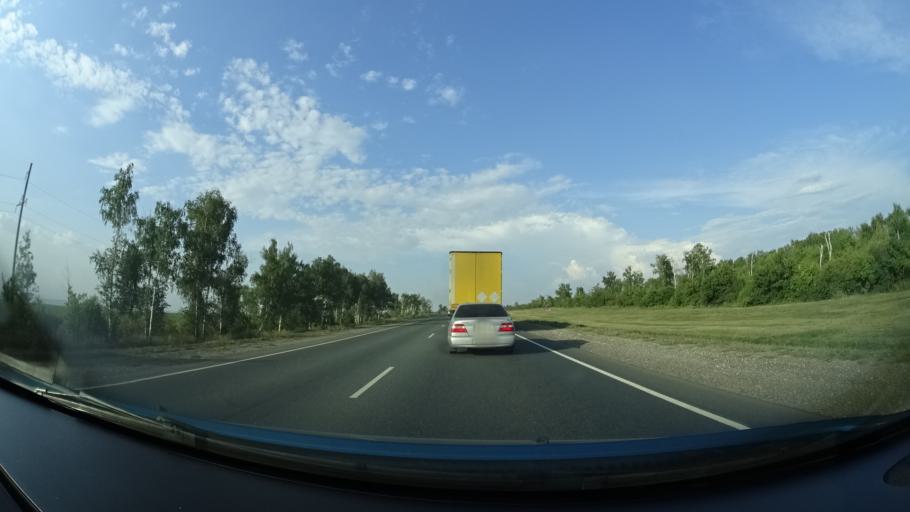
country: RU
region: Samara
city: Krasnyy Yar
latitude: 53.6689
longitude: 50.7642
